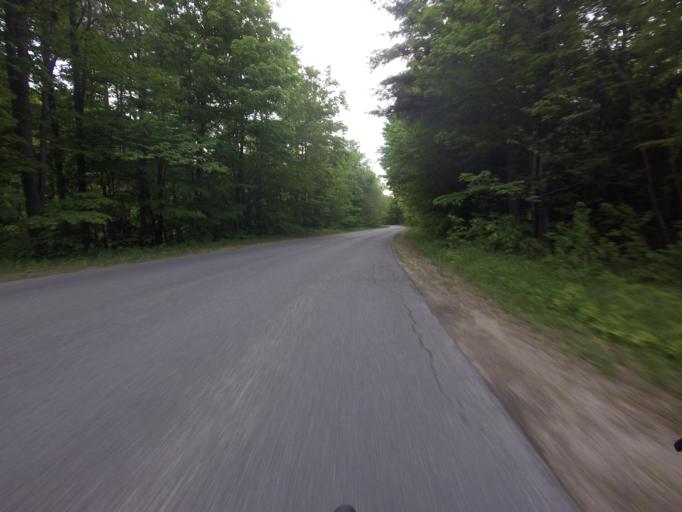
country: US
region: New York
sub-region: St. Lawrence County
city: Gouverneur
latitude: 44.1518
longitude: -75.3597
